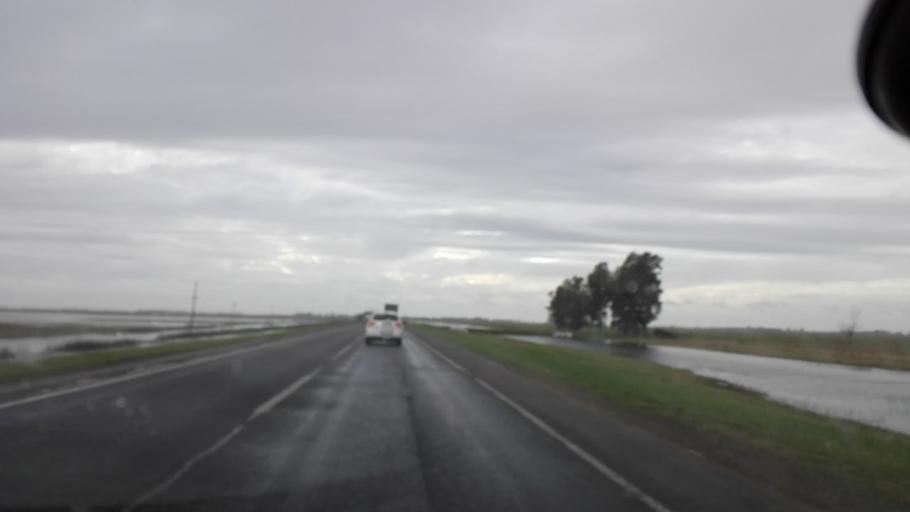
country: AR
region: Buenos Aires
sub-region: Partido de Las Flores
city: Las Flores
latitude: -35.7490
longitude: -58.9232
